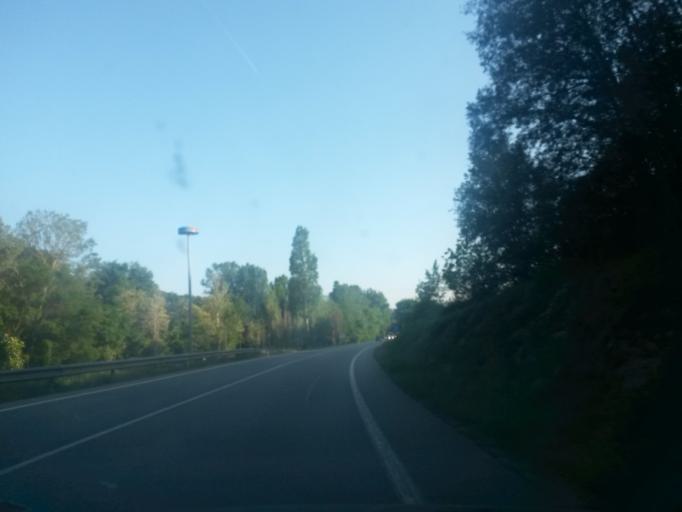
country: ES
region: Catalonia
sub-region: Provincia de Girona
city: Porqueres
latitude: 42.1625
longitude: 2.7458
